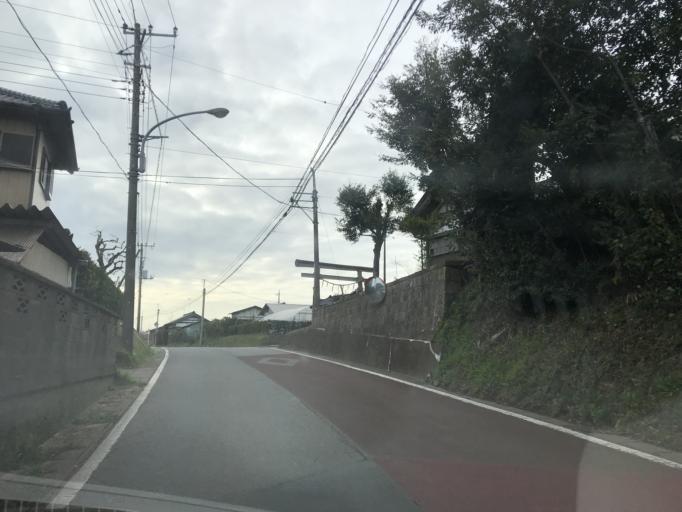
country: JP
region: Chiba
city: Omigawa
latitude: 35.7933
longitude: 140.6017
